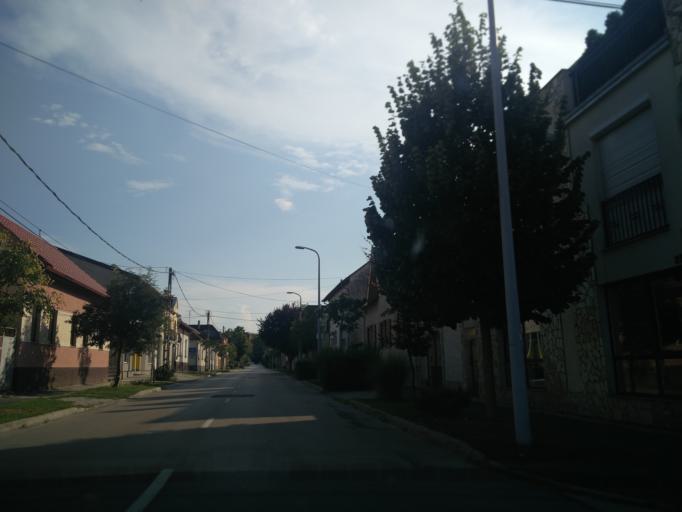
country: HU
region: Zala
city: Zalaegerszeg
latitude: 46.8444
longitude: 16.8353
